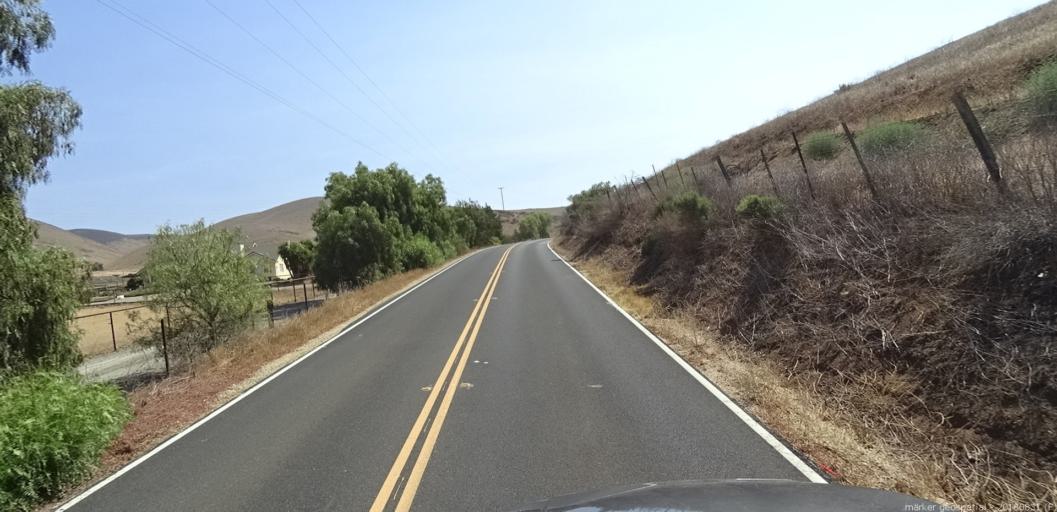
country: US
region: California
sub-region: Monterey County
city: Soledad
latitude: 36.4159
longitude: -121.2672
